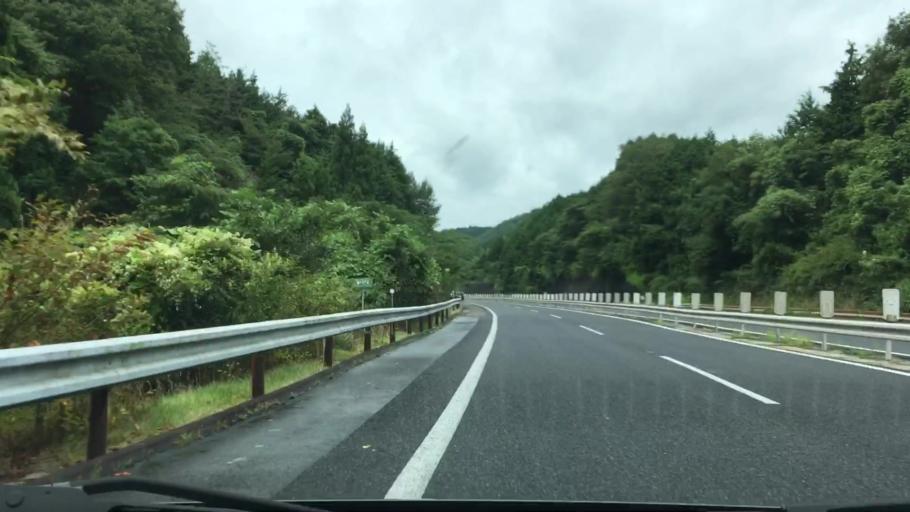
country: JP
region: Hyogo
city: Yamazakicho-nakabirose
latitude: 35.0135
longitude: 134.2809
